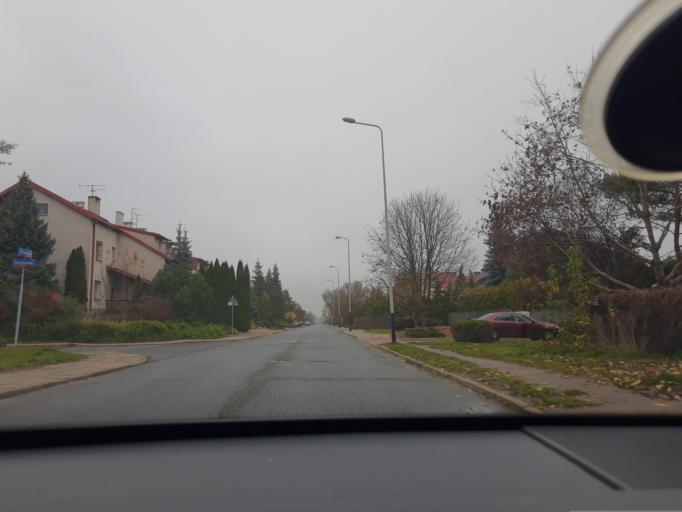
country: PL
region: Lodz Voivodeship
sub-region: Powiat pabianicki
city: Konstantynow Lodzki
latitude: 51.7394
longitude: 19.3796
